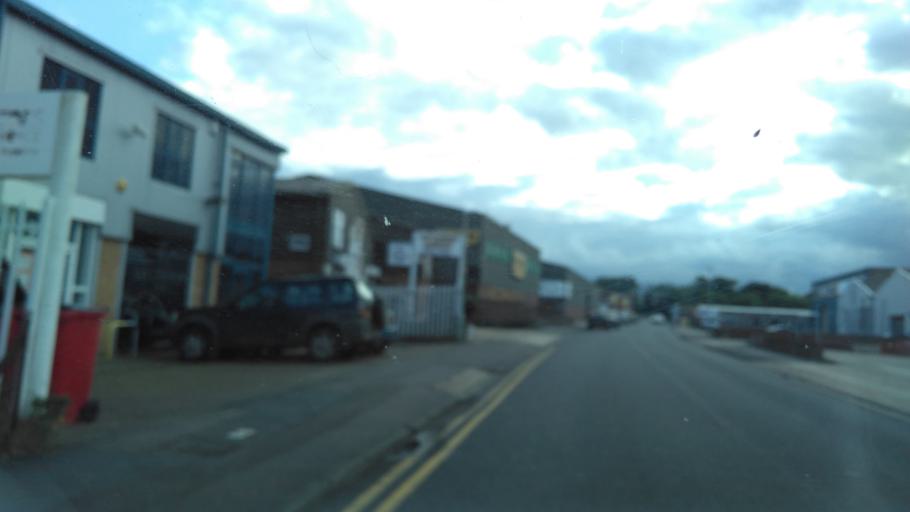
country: GB
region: England
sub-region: Kent
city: Canterbury
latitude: 51.2737
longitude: 1.0702
